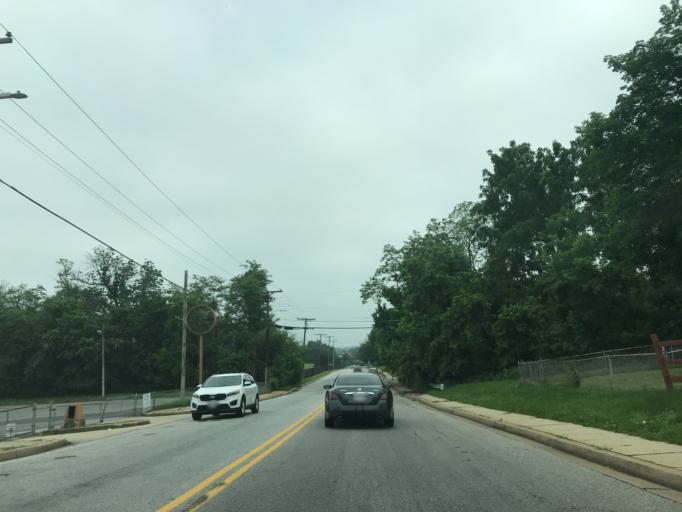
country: US
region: Maryland
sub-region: Baltimore County
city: Charlestown
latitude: 39.2725
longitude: -76.6929
